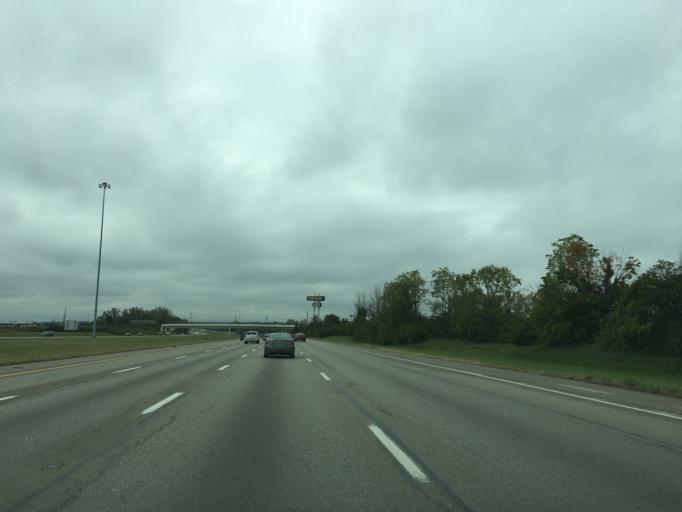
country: US
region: Ohio
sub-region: Butler County
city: Beckett Ridge
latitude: 39.3190
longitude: -84.4280
